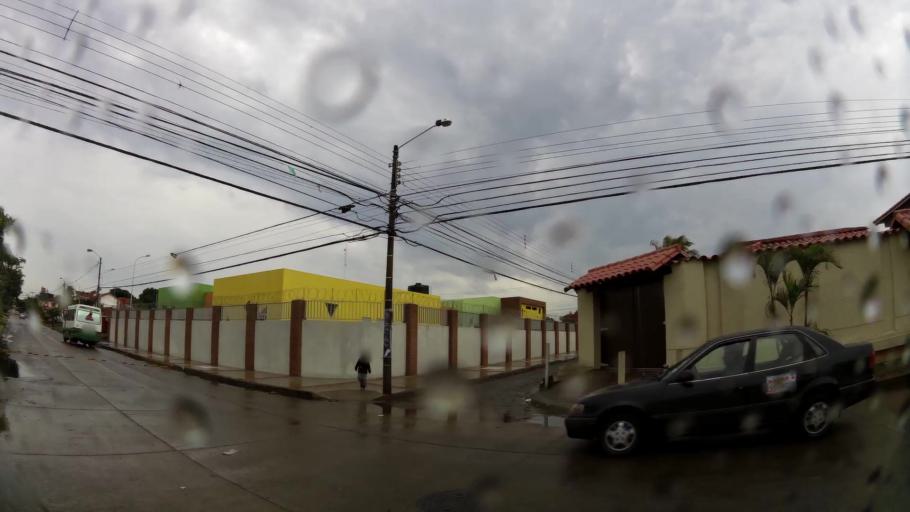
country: BO
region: Santa Cruz
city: Santa Cruz de la Sierra
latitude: -17.7616
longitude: -63.1553
